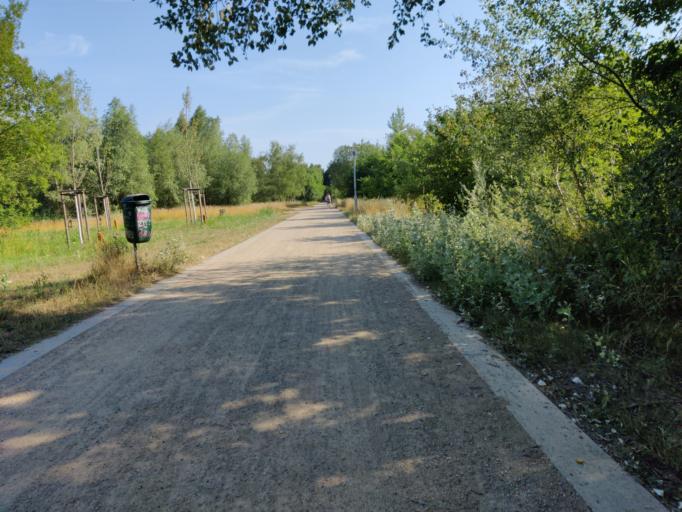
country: DE
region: Saxony
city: Markkleeberg
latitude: 51.2896
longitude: 12.3521
